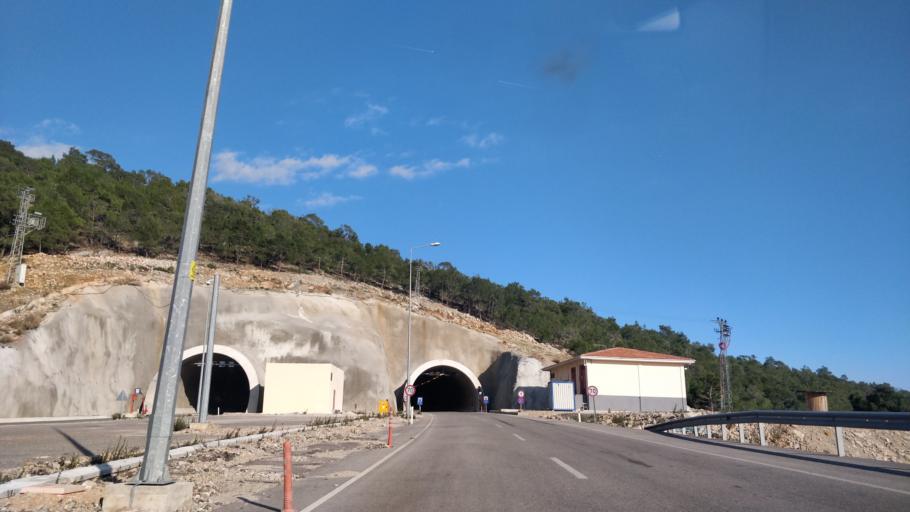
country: TR
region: Mersin
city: Ovacik
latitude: 36.1656
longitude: 33.5762
